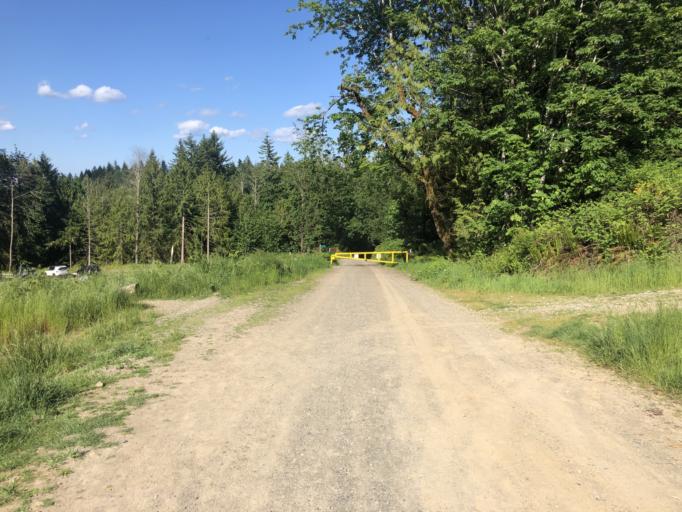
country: US
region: Washington
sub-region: Kitsap County
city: Erlands Point-Kitsap Lake
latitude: 47.5796
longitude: -122.7186
